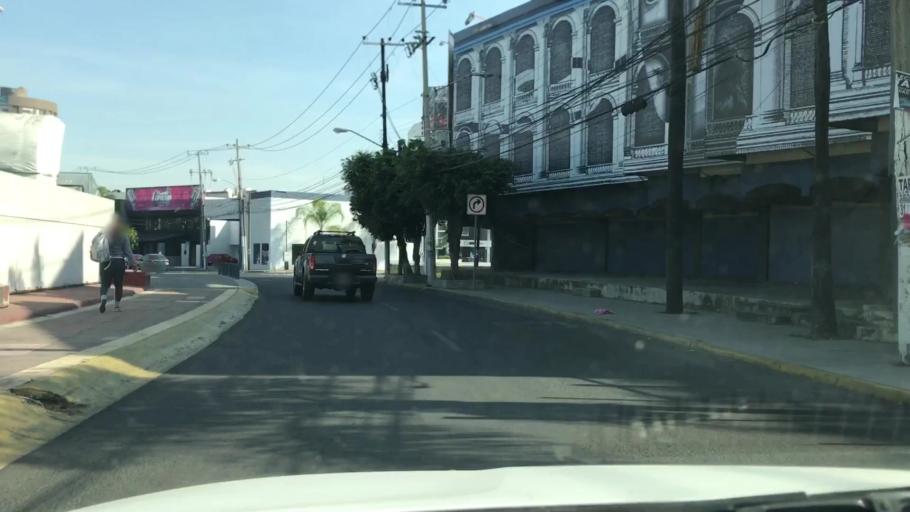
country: MX
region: Jalisco
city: Guadalajara
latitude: 20.6460
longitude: -103.4054
